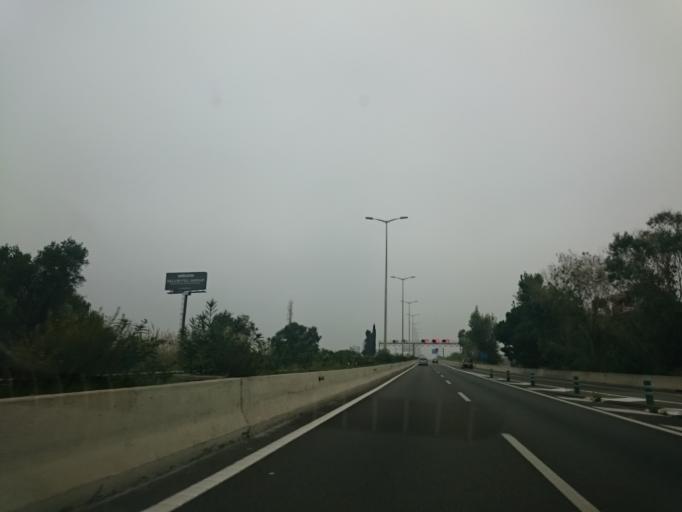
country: ES
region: Catalonia
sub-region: Provincia de Barcelona
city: El Prat de Llobregat
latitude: 41.3228
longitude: 2.0757
